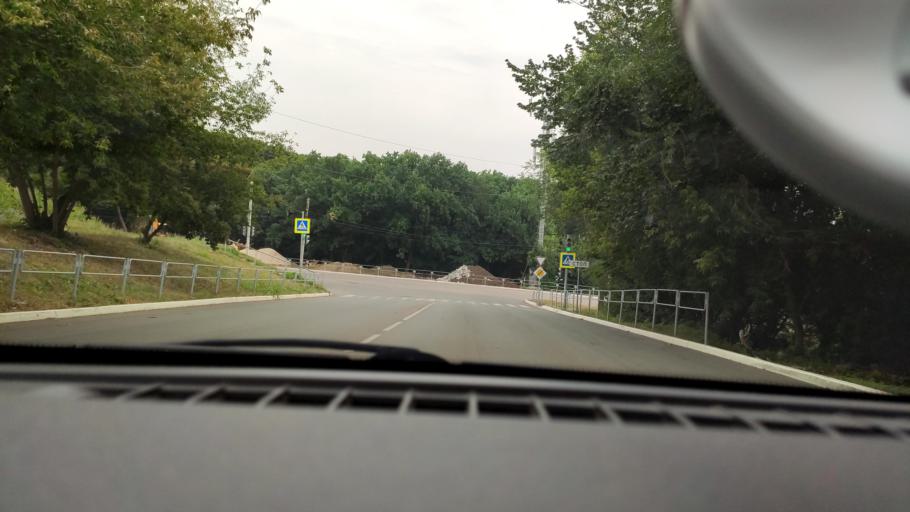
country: RU
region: Samara
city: Novokuybyshevsk
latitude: 53.0988
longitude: 49.9824
